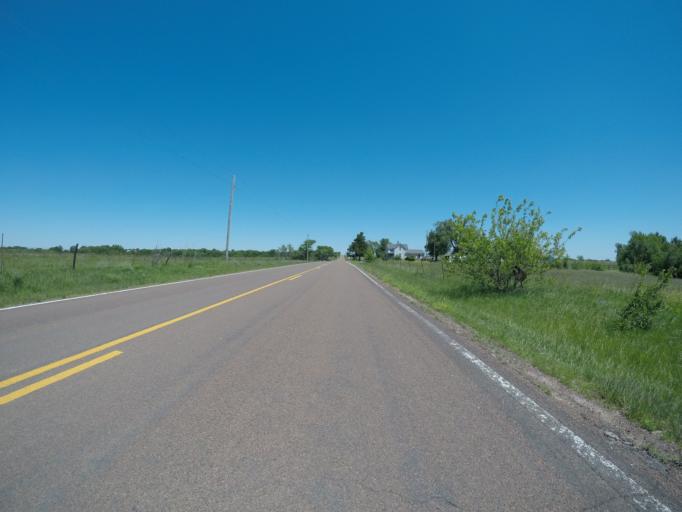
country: US
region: Kansas
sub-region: Shawnee County
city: Auburn
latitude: 38.9166
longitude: -95.9280
